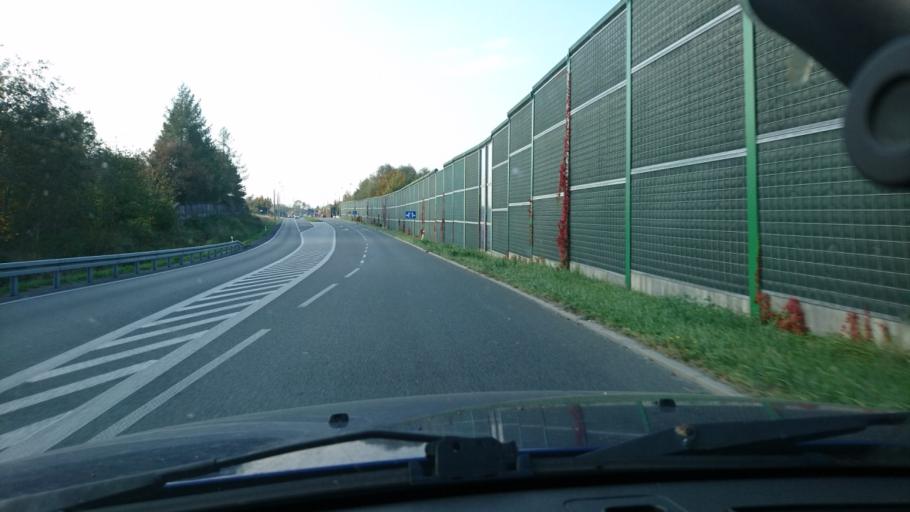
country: PL
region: Silesian Voivodeship
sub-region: Powiat cieszynski
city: Ustron
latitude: 49.7155
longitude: 18.8044
